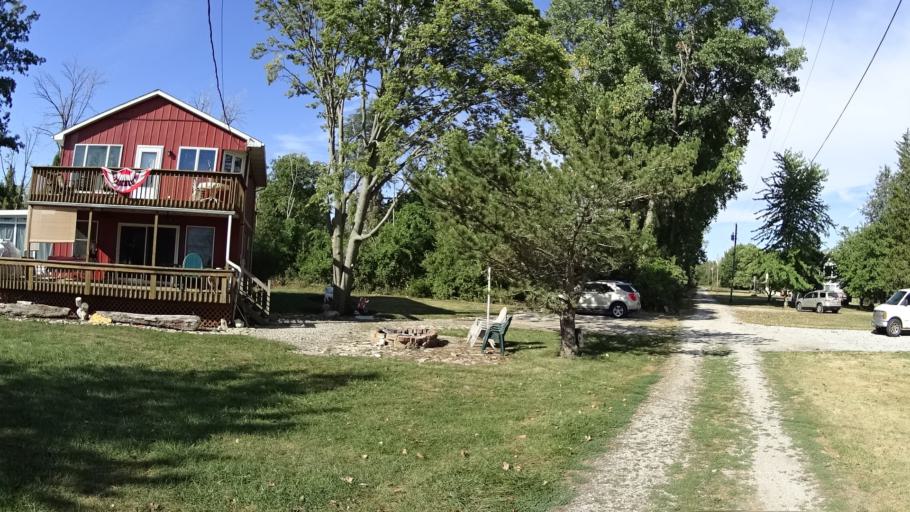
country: US
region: Ohio
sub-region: Erie County
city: Sandusky
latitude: 41.6090
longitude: -82.6808
